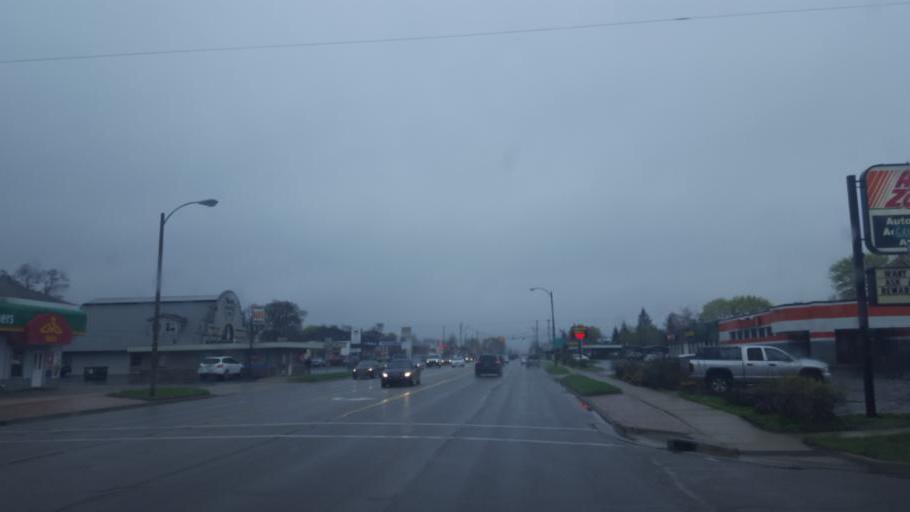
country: US
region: Michigan
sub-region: Isabella County
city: Mount Pleasant
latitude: 43.5955
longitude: -84.7677
